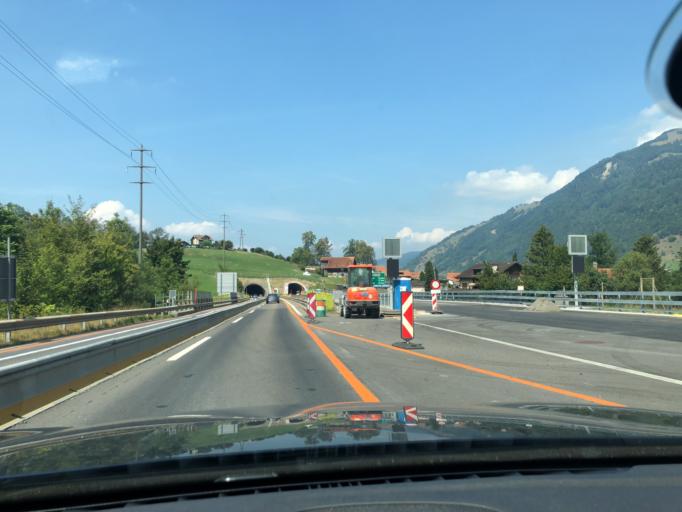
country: CH
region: Schwyz
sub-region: Bezirk Schwyz
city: Goldau
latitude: 47.0457
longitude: 8.5436
